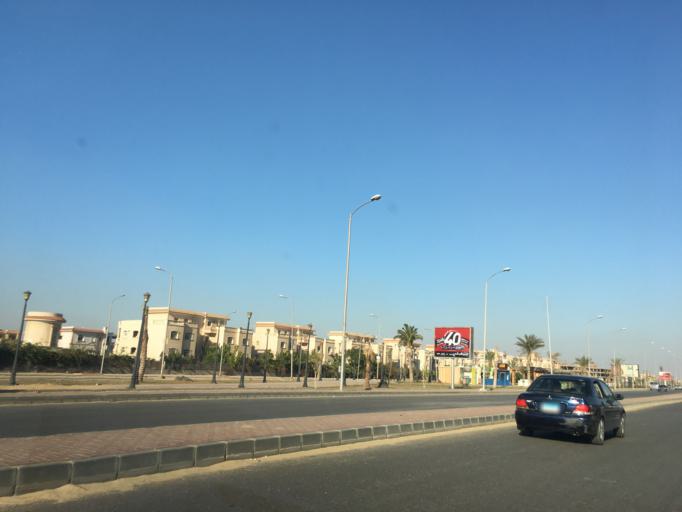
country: EG
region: Al Jizah
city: Madinat Sittah Uktubar
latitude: 30.0042
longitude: 30.9654
